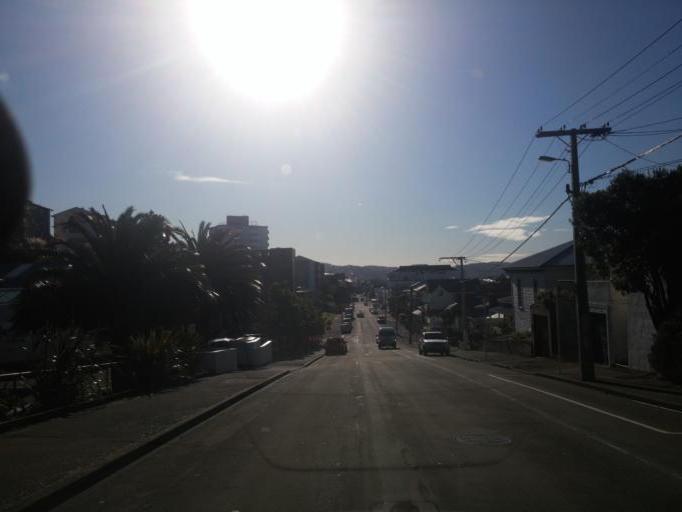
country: NZ
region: Wellington
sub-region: Wellington City
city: Wellington
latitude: -41.3099
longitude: 174.7759
